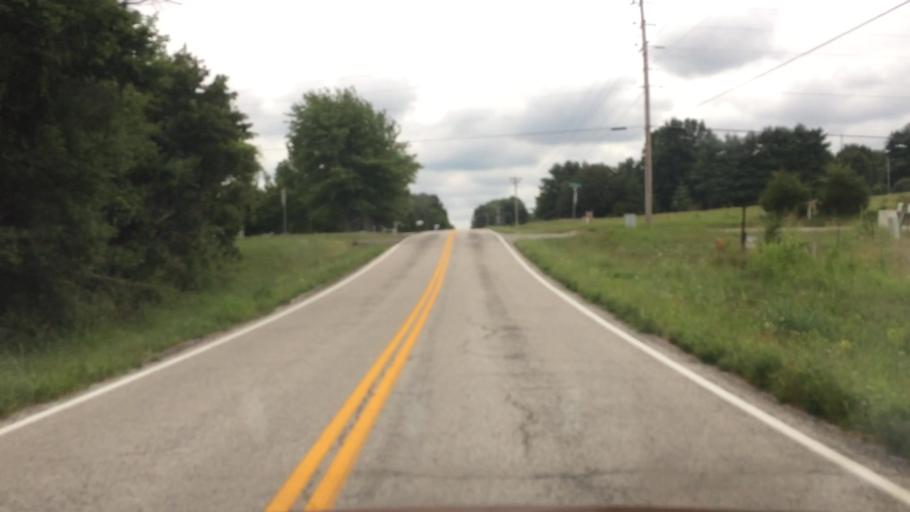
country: US
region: Missouri
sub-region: Greene County
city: Strafford
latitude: 37.2942
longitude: -93.2050
